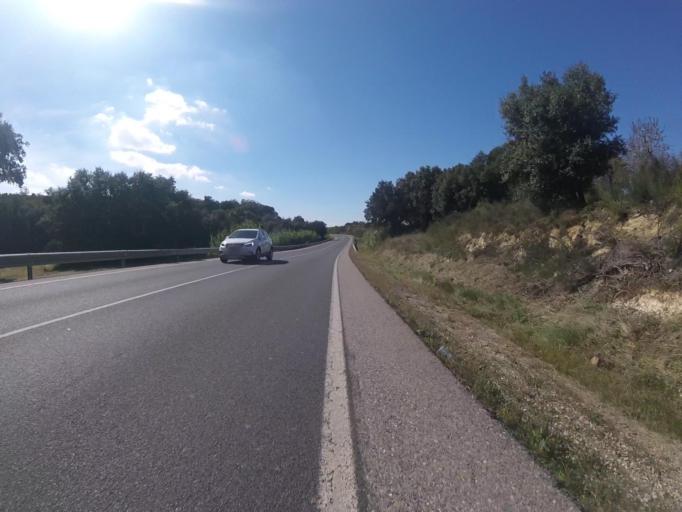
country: ES
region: Valencia
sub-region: Provincia de Castello
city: Sarratella
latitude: 40.3323
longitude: -0.0142
